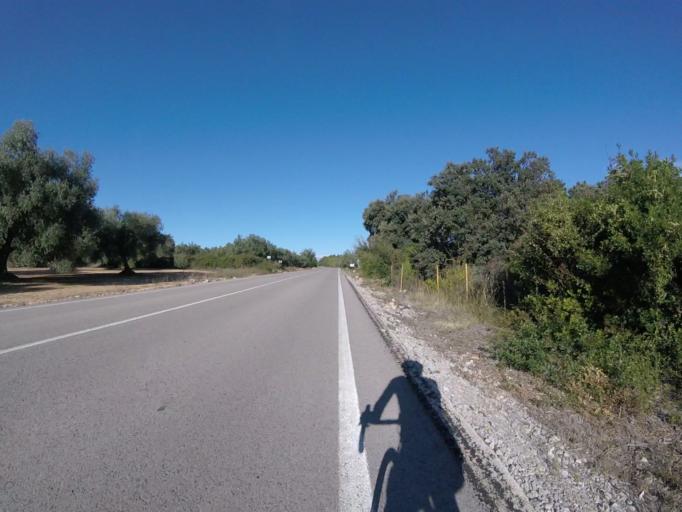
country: ES
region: Valencia
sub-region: Provincia de Castello
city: Cervera del Maestre
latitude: 40.4745
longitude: 0.2299
